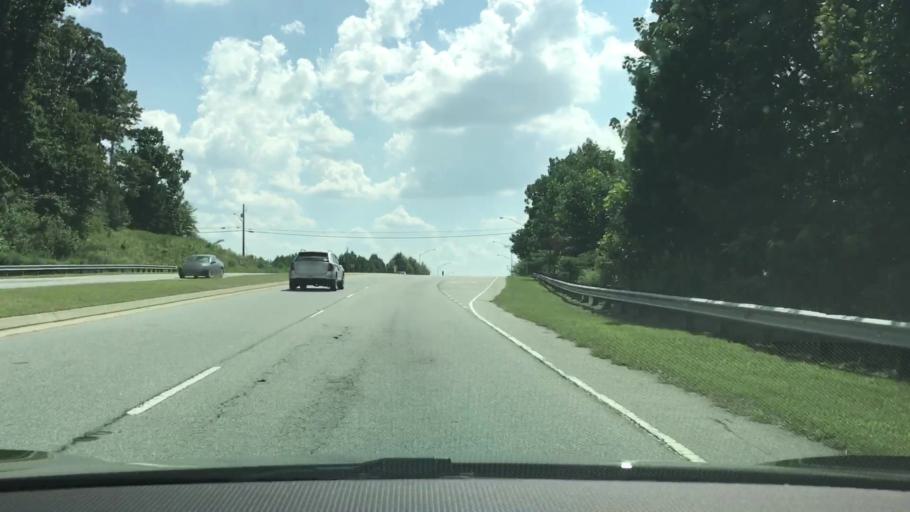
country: US
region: Georgia
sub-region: Gwinnett County
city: Buford
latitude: 34.0841
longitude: -84.0021
